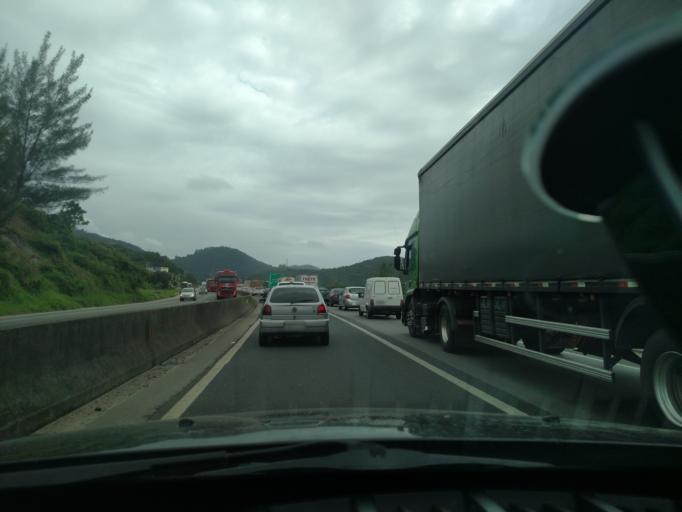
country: BR
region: Santa Catarina
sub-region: Itapema
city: Itapema
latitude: -27.0703
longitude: -48.5955
